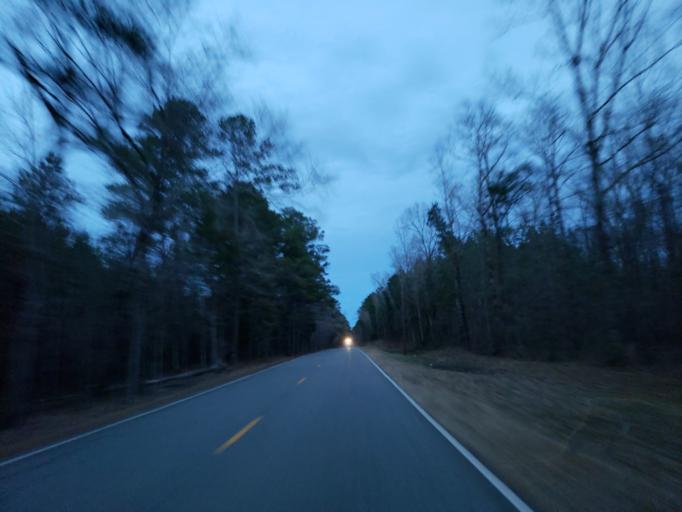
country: US
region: Alabama
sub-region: Greene County
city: Eutaw
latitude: 32.8823
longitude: -88.0645
